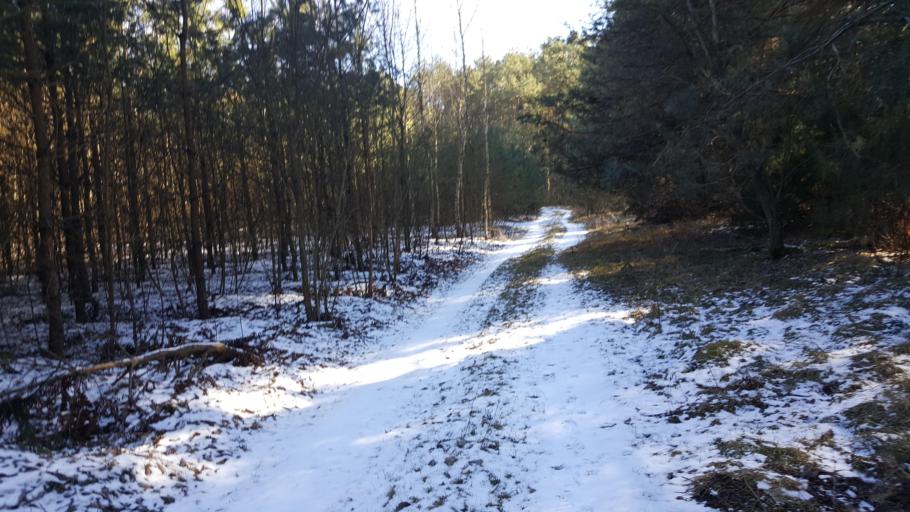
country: BY
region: Brest
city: Kamyanyets
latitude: 52.3672
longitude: 23.8191
